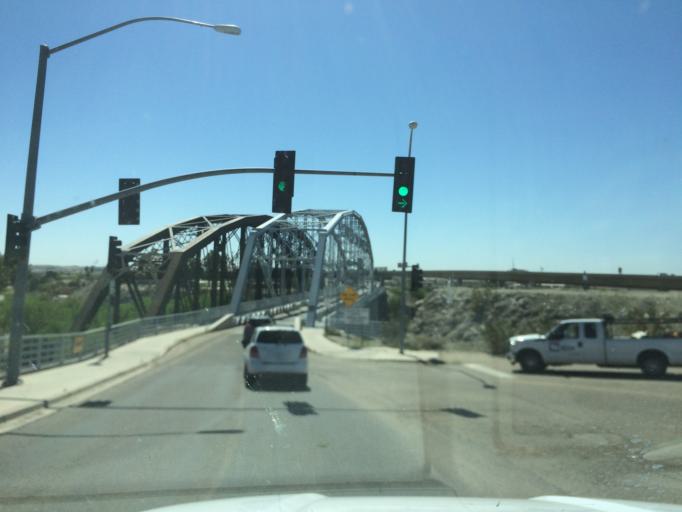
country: US
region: Arizona
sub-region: Yuma County
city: Yuma
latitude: 32.7295
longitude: -114.6157
